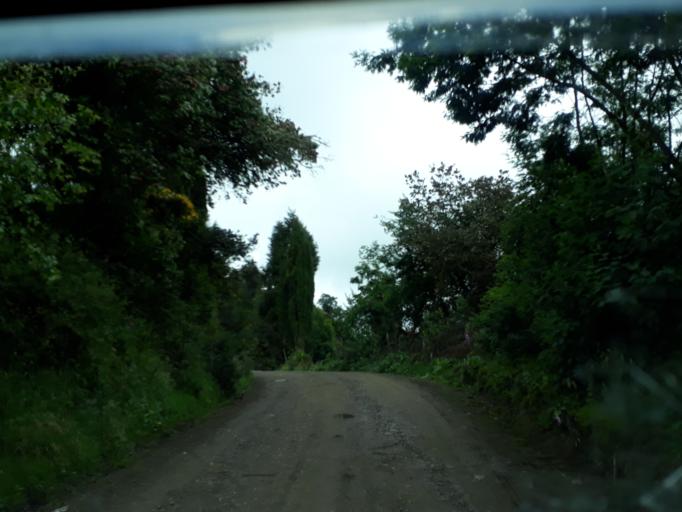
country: CO
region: Cundinamarca
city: Cogua
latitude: 5.1630
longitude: -73.9934
